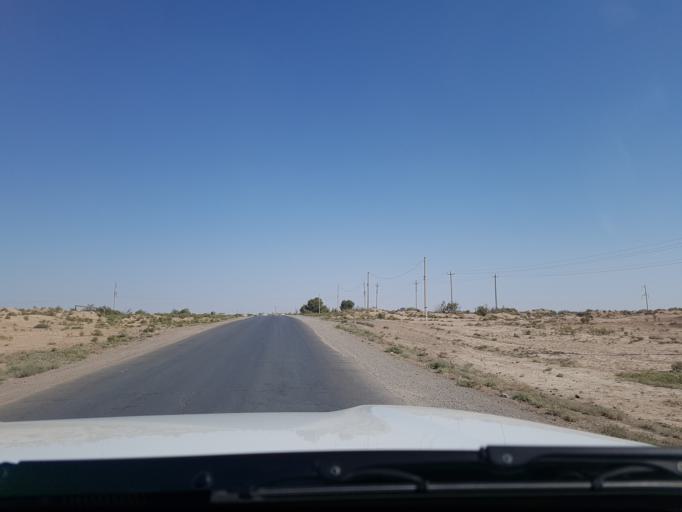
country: IR
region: Razavi Khorasan
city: Sarakhs
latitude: 36.5225
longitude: 61.2420
